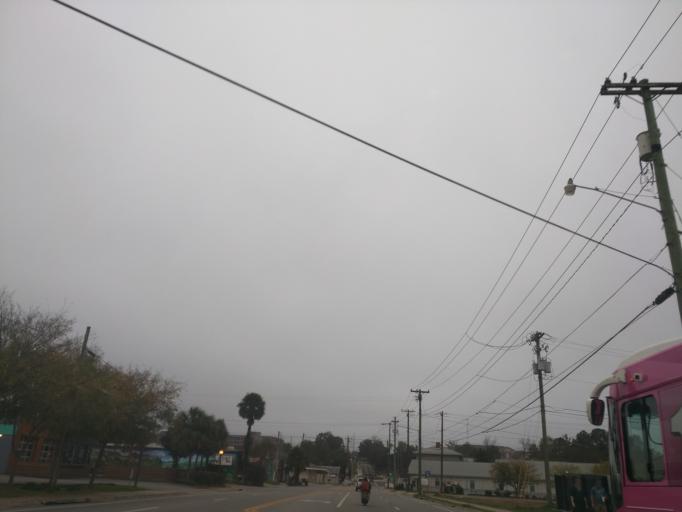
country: US
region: Florida
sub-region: Leon County
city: Tallahassee
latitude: 30.4351
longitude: -84.2897
